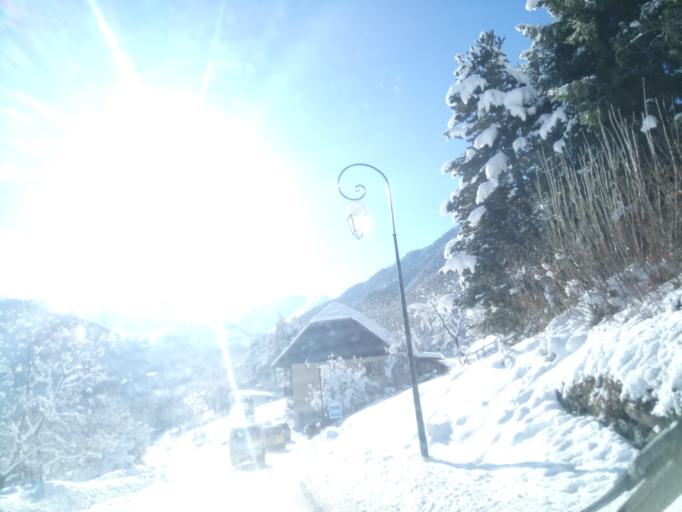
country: FR
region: Rhone-Alpes
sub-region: Departement de la Savoie
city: Saint-Jean-de-Maurienne
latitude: 45.2452
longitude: 6.3099
